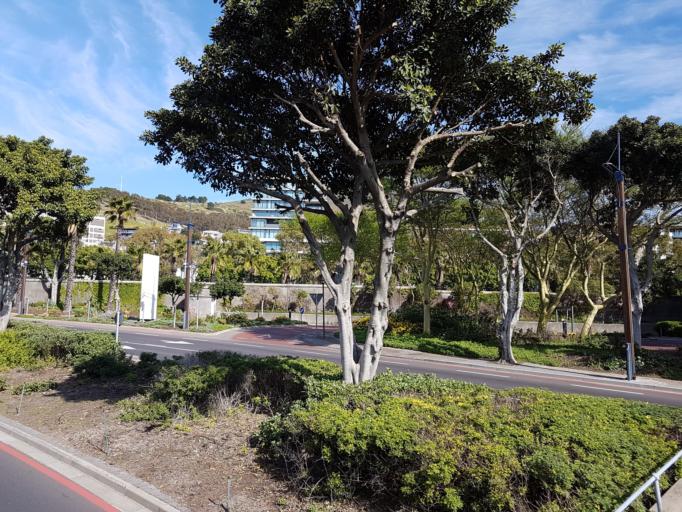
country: ZA
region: Western Cape
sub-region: City of Cape Town
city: Cape Town
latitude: -33.9094
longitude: 18.4151
